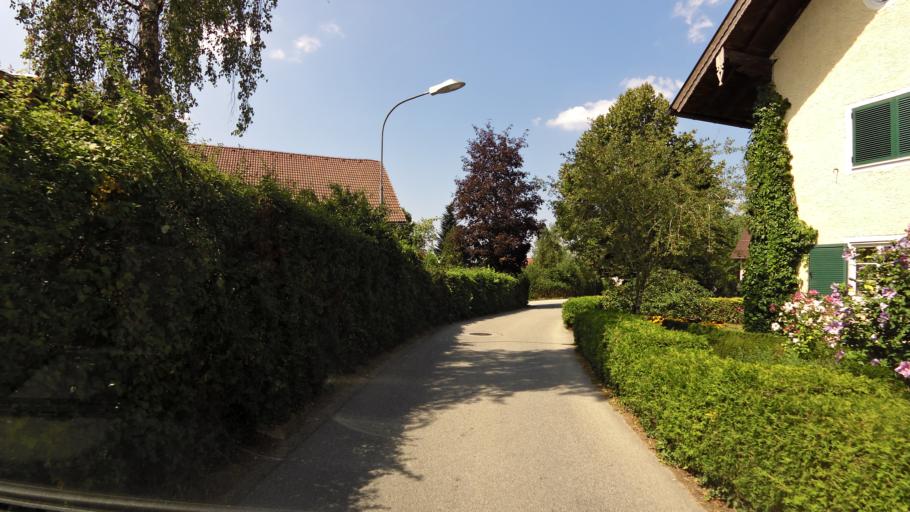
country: AT
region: Salzburg
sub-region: Politischer Bezirk Salzburg-Umgebung
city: Henndorf am Wallersee
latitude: 47.8970
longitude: 13.1905
